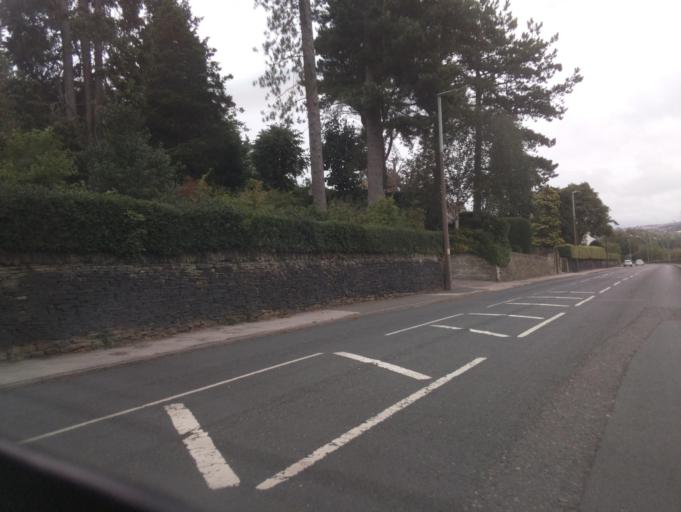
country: GB
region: England
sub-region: Kirklees
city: Holmfirth
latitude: 53.5627
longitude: -1.8069
